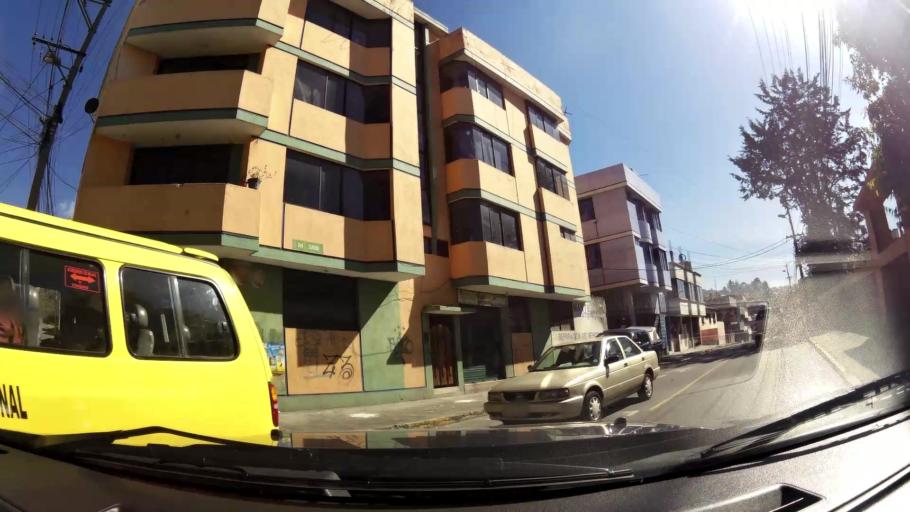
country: EC
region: Pichincha
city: Quito
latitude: -0.2400
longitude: -78.5340
